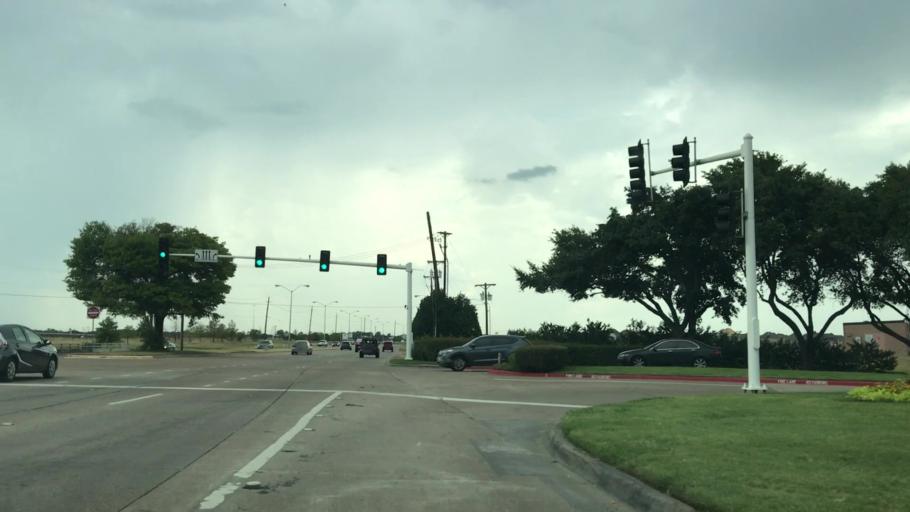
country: US
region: Texas
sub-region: Dallas County
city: Farmers Branch
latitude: 32.9094
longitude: -96.9222
